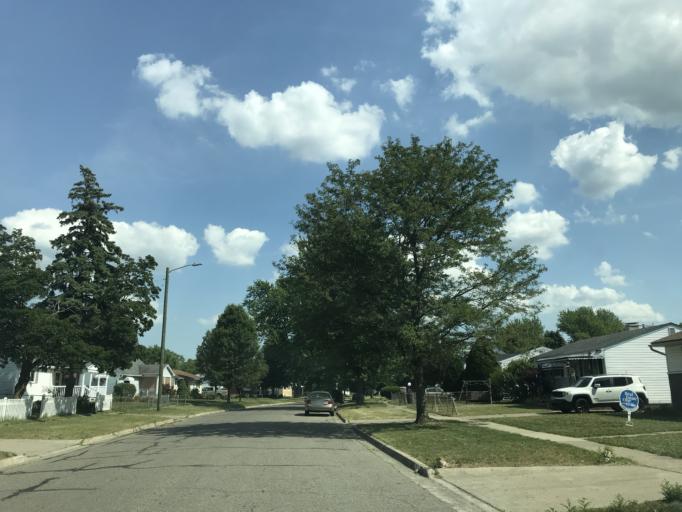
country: US
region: Michigan
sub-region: Washtenaw County
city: Ypsilanti
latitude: 42.2567
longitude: -83.5833
